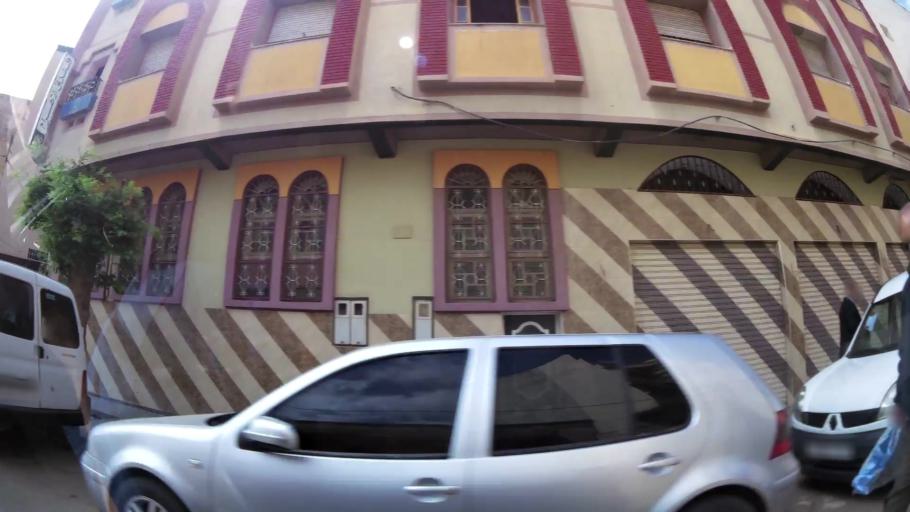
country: MA
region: Oriental
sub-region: Oujda-Angad
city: Oujda
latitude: 34.6832
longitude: -1.9121
